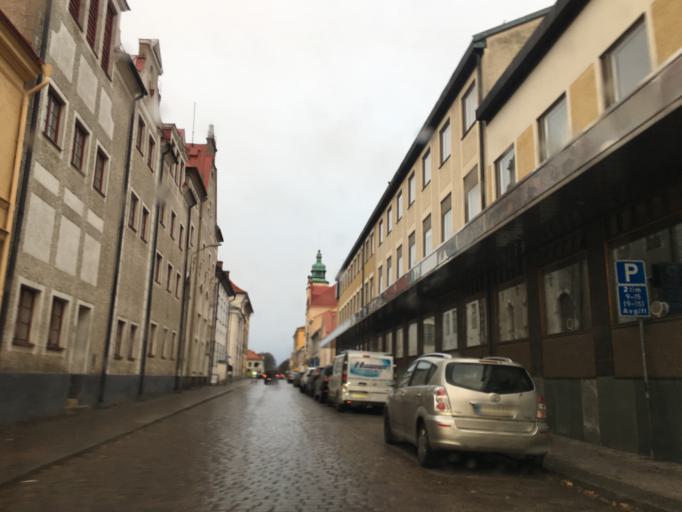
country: SE
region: Kalmar
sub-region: Kalmar Kommun
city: Kalmar
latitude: 56.6632
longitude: 16.3674
